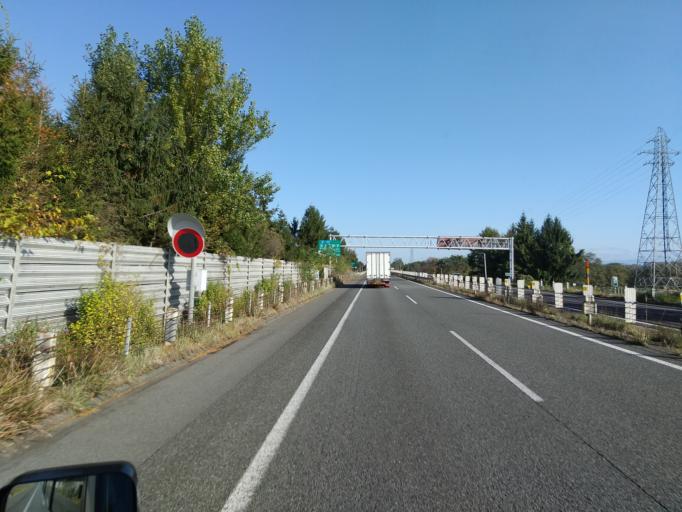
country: JP
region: Iwate
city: Kitakami
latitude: 39.2832
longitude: 141.0808
